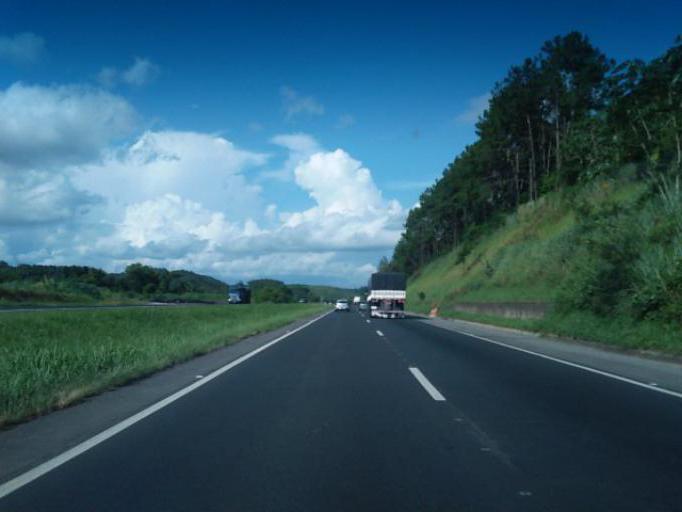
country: BR
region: Sao Paulo
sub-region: Registro
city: Registro
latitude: -24.4282
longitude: -47.7840
